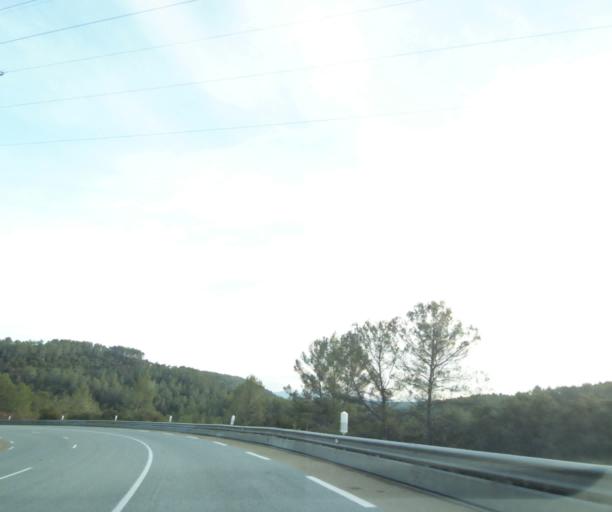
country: FR
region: Provence-Alpes-Cote d'Azur
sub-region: Departement du Var
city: Trans-en-Provence
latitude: 43.5041
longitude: 6.5091
